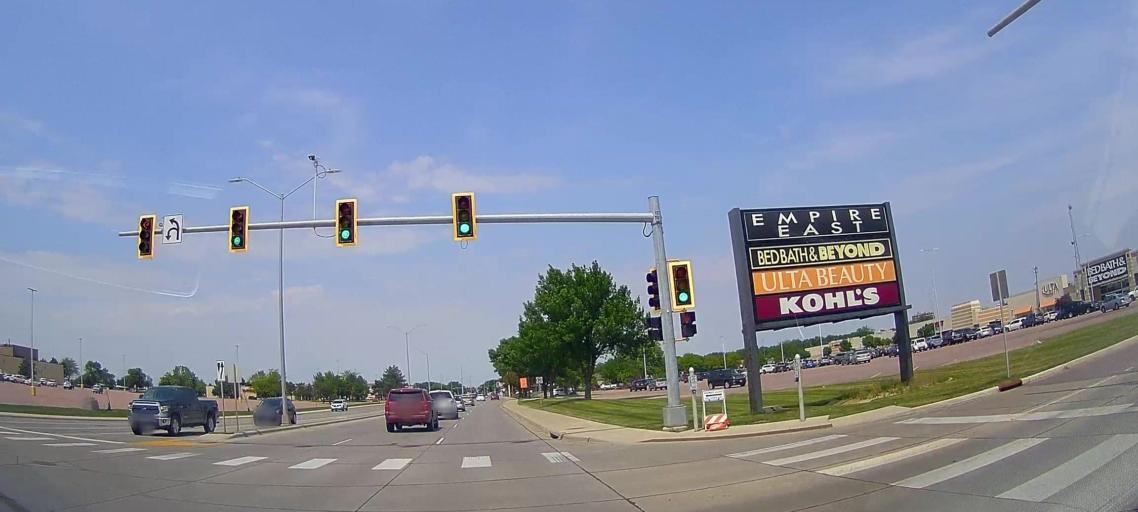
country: US
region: South Dakota
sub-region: Minnehaha County
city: Sioux Falls
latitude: 43.5100
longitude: -96.7712
